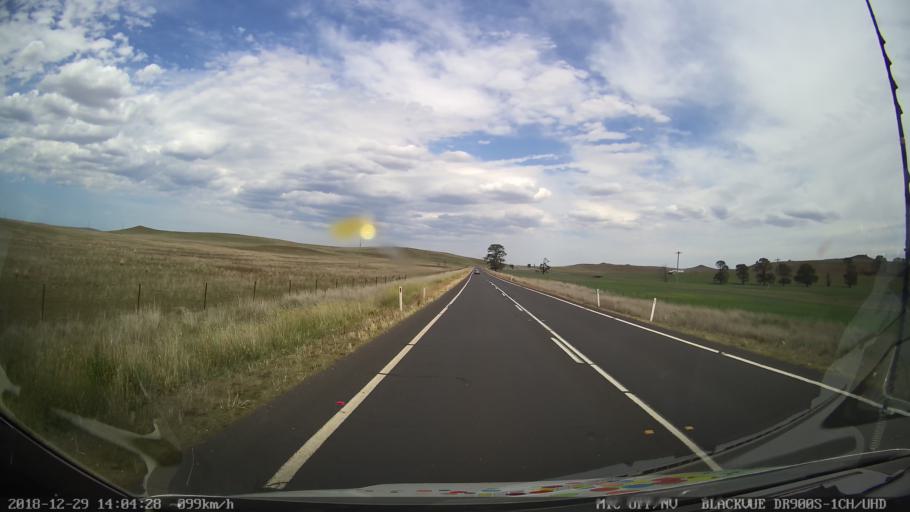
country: AU
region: New South Wales
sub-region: Cooma-Monaro
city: Cooma
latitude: -36.3166
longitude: 149.1868
